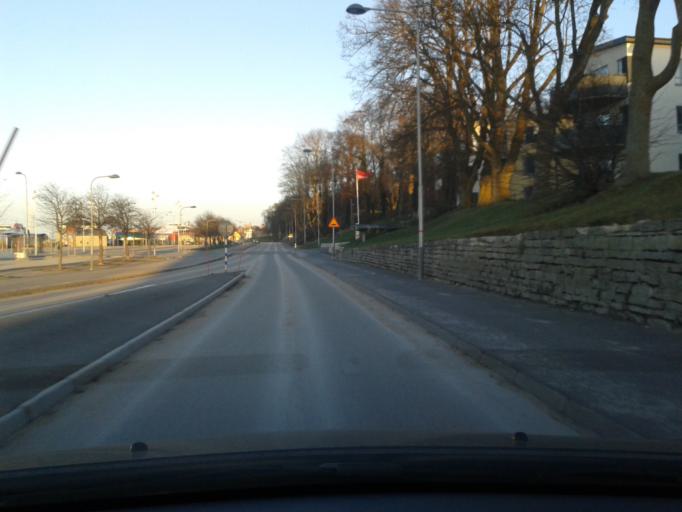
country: SE
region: Gotland
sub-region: Gotland
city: Visby
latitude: 57.6330
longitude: 18.2807
